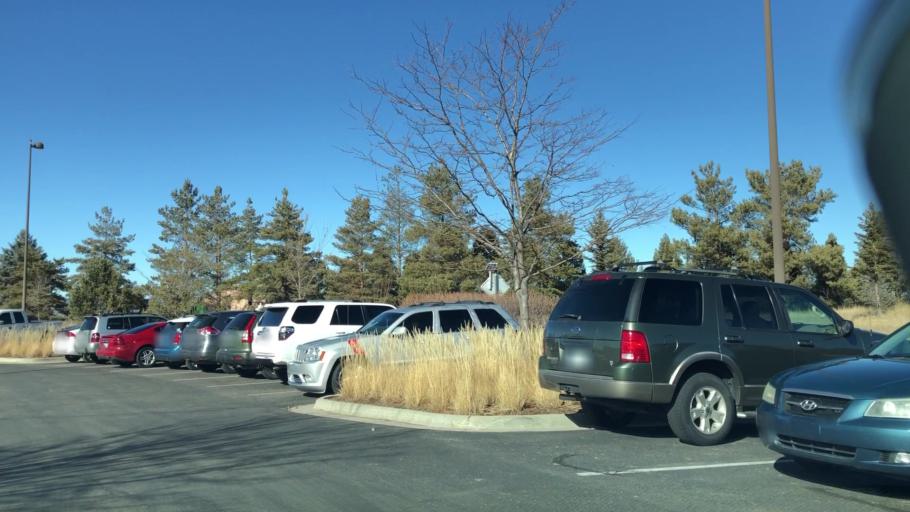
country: US
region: Colorado
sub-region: Larimer County
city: Loveland
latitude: 40.4173
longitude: -104.9959
